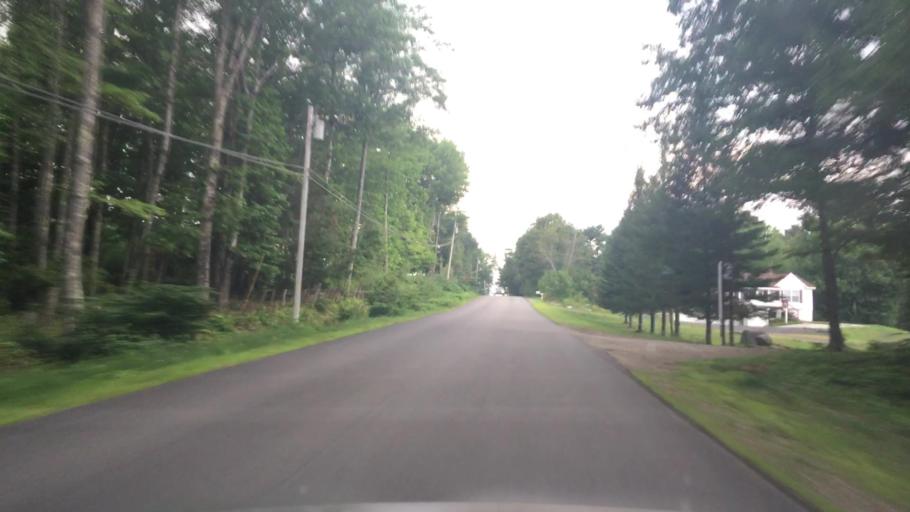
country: US
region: Maine
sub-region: Knox County
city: Washington
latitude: 44.3812
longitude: -69.3524
